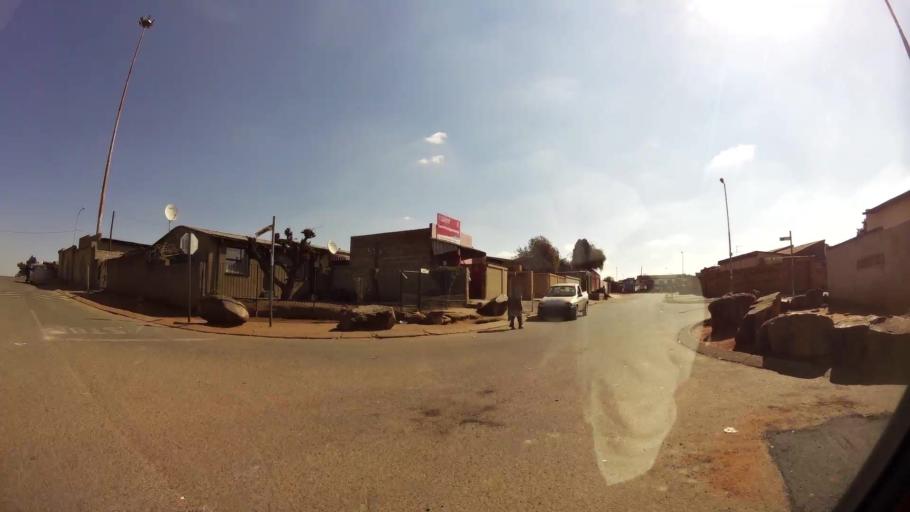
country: ZA
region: Gauteng
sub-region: City of Johannesburg Metropolitan Municipality
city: Soweto
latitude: -26.2350
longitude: 27.8837
